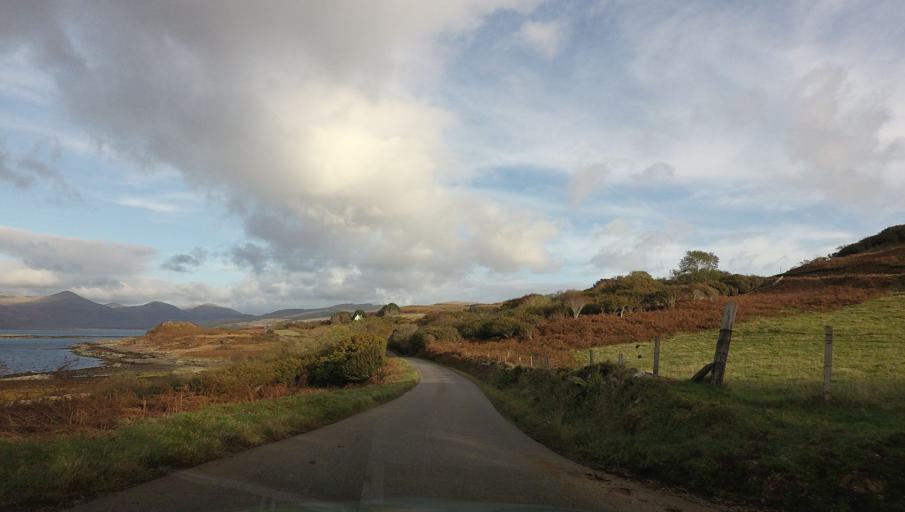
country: GB
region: Scotland
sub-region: Argyll and Bute
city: Isle Of Mull
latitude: 56.3527
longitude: -6.0796
